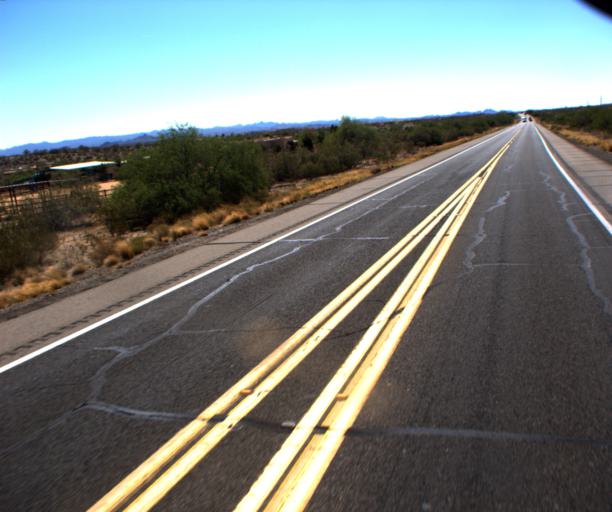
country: US
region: Arizona
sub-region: Maricopa County
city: Wickenburg
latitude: 34.0371
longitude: -112.8266
